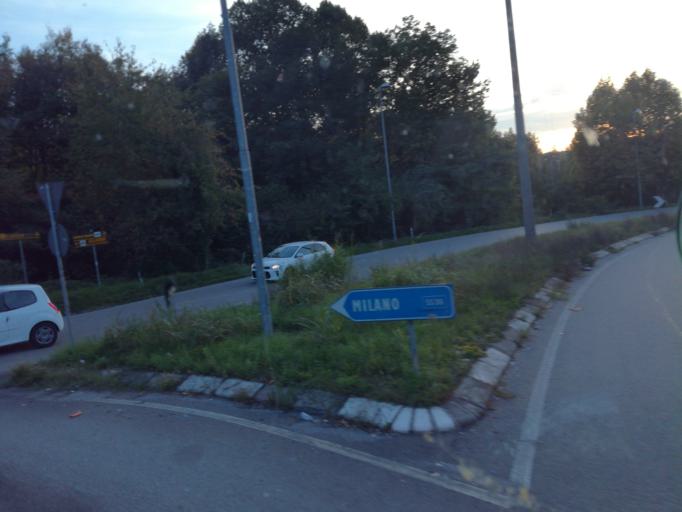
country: IT
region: Lombardy
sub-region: Provincia di Lecco
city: Nibionno
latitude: 45.7486
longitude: 9.2619
